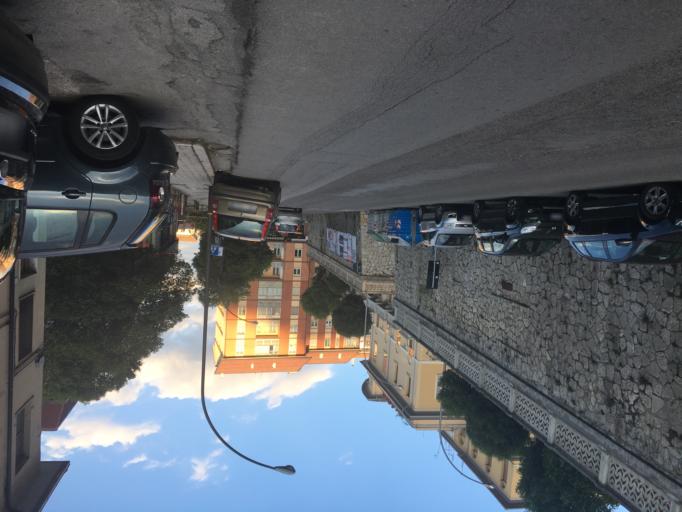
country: IT
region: Basilicate
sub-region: Provincia di Potenza
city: Potenza
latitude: 40.6354
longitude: 15.8048
